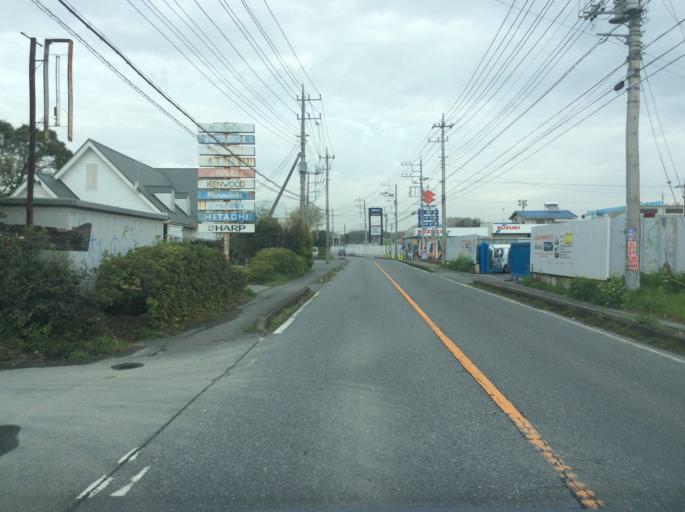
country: JP
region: Ibaraki
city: Iwai
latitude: 36.0159
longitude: 139.9063
